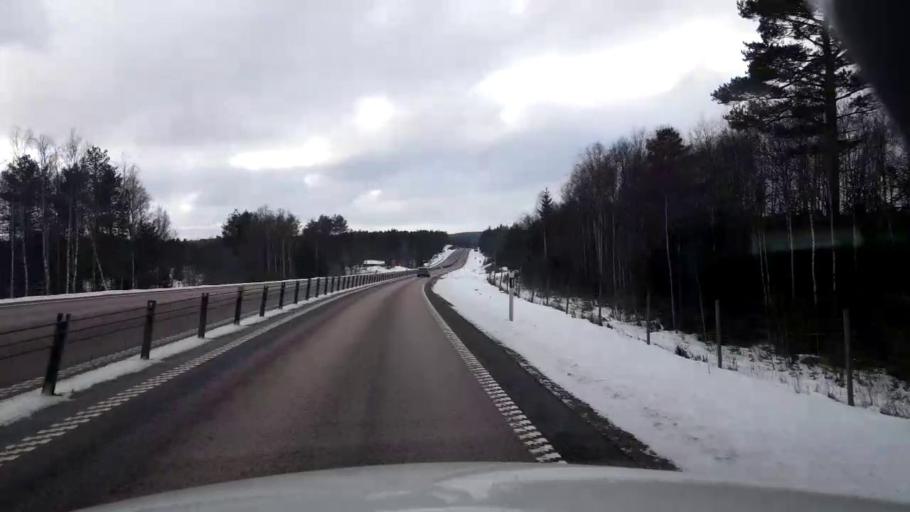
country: SE
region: Gaevleborg
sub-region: Hudiksvalls Kommun
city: Hudiksvall
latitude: 61.8103
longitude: 17.1866
